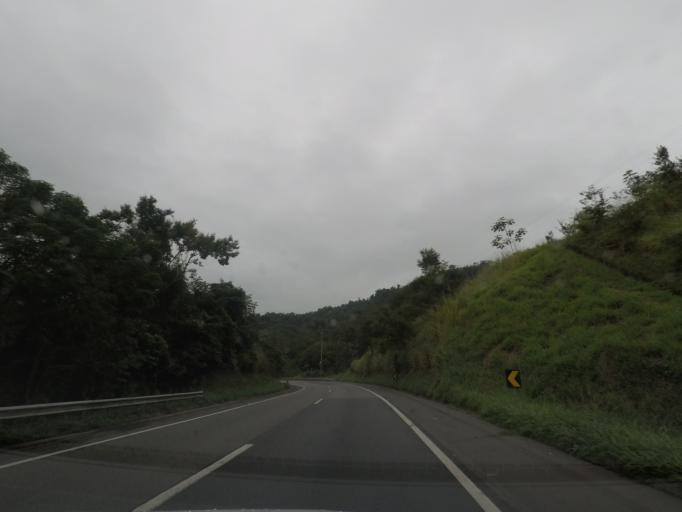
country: BR
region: Sao Paulo
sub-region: Cajati
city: Cajati
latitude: -24.7905
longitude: -48.2057
